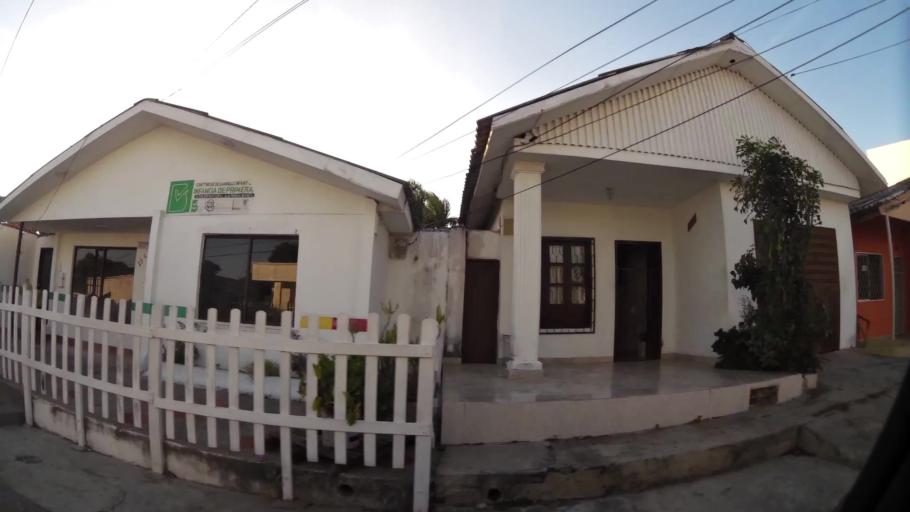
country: CO
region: Atlantico
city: Barranquilla
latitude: 10.9727
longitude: -74.8127
